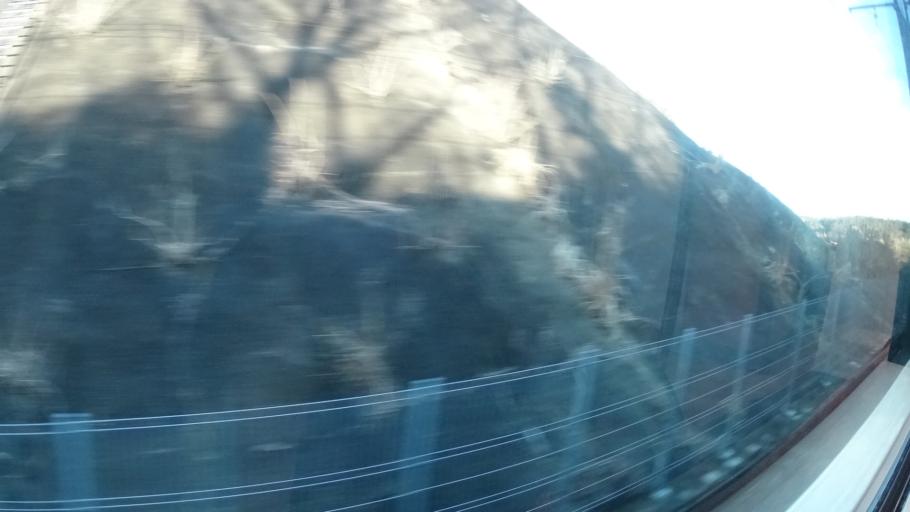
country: JP
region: Fukushima
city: Namie
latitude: 37.3839
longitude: 140.9902
